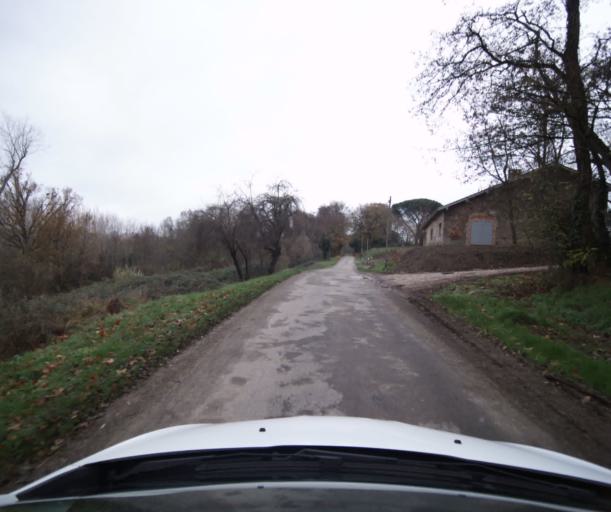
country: FR
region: Midi-Pyrenees
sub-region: Departement du Tarn-et-Garonne
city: Moissac
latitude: 44.0748
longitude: 1.1316
